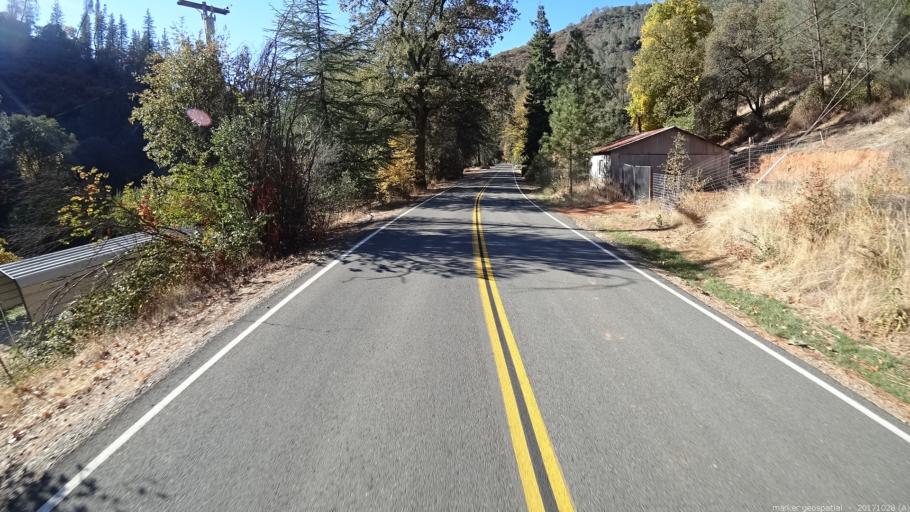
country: US
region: California
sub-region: Trinity County
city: Lewiston
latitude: 40.7356
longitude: -122.6247
